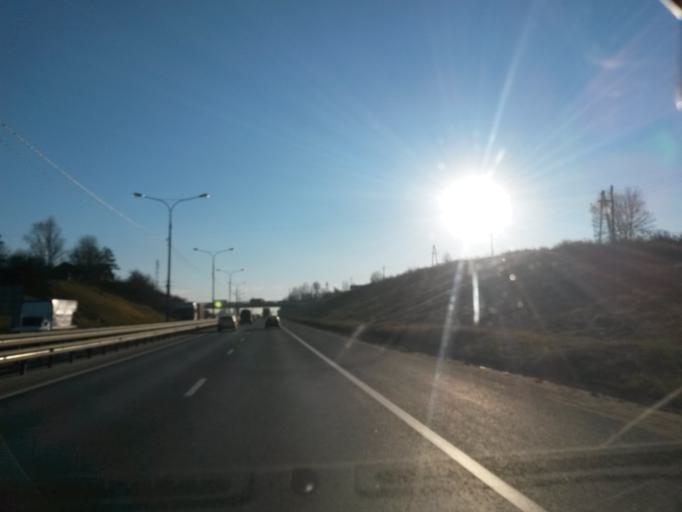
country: RU
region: Moskovskaya
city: Lesnyye Polyany
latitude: 55.9897
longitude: 37.8726
